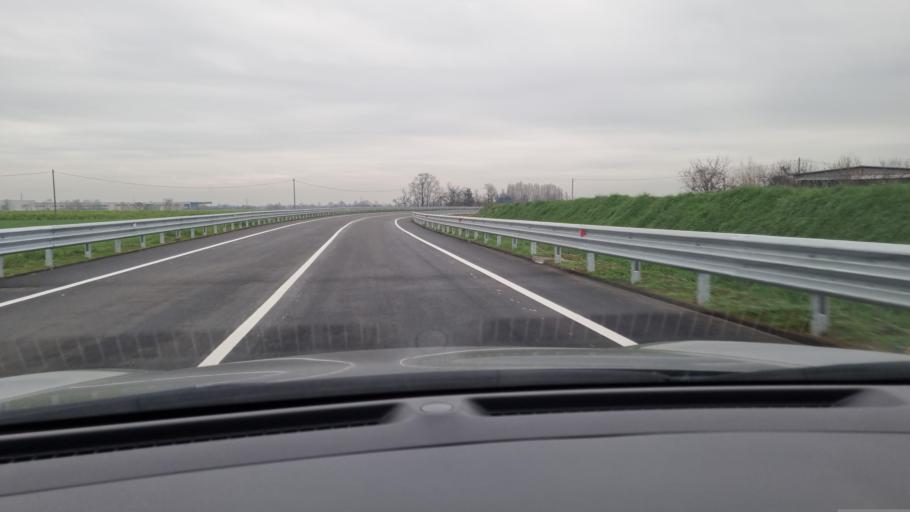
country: IT
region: Lombardy
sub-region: Provincia di Bergamo
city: Verdello
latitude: 45.6097
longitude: 9.6399
